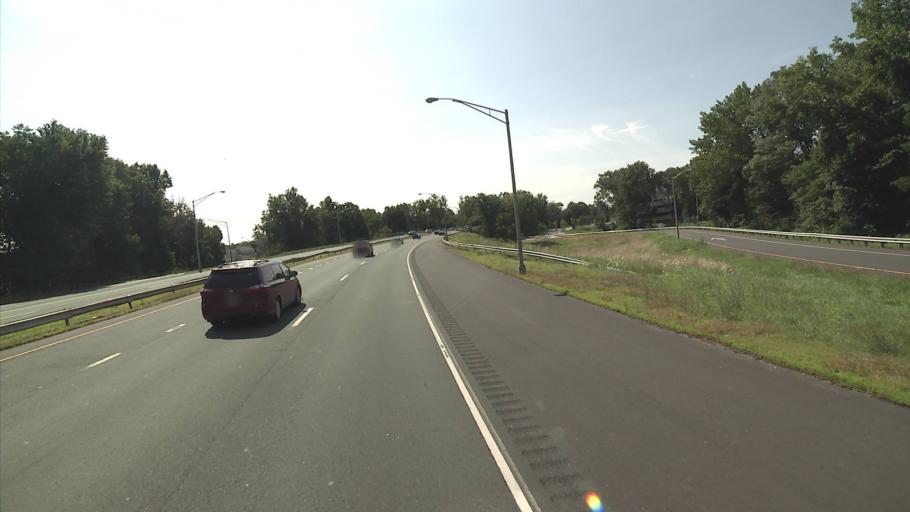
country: US
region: Connecticut
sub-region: Hartford County
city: Wethersfield
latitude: 41.7519
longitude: -72.6438
